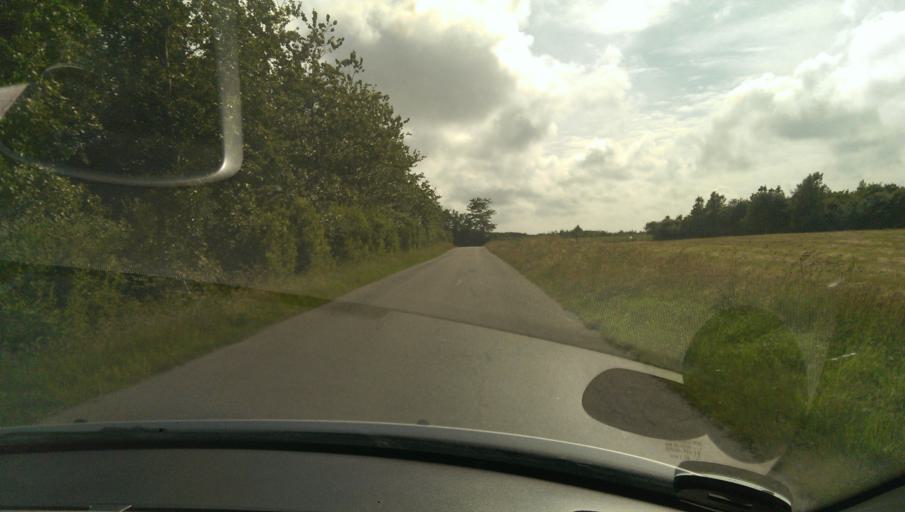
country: DK
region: Central Jutland
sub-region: Holstebro Kommune
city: Ulfborg
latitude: 56.2764
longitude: 8.2703
